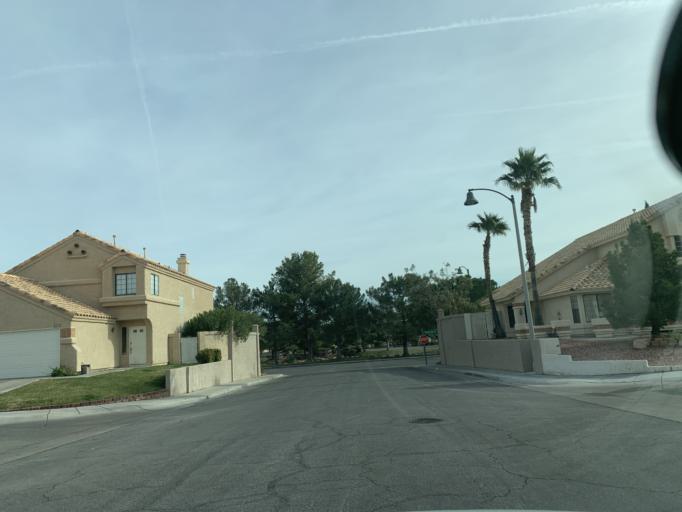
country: US
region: Nevada
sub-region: Clark County
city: Summerlin South
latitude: 36.1342
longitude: -115.3029
